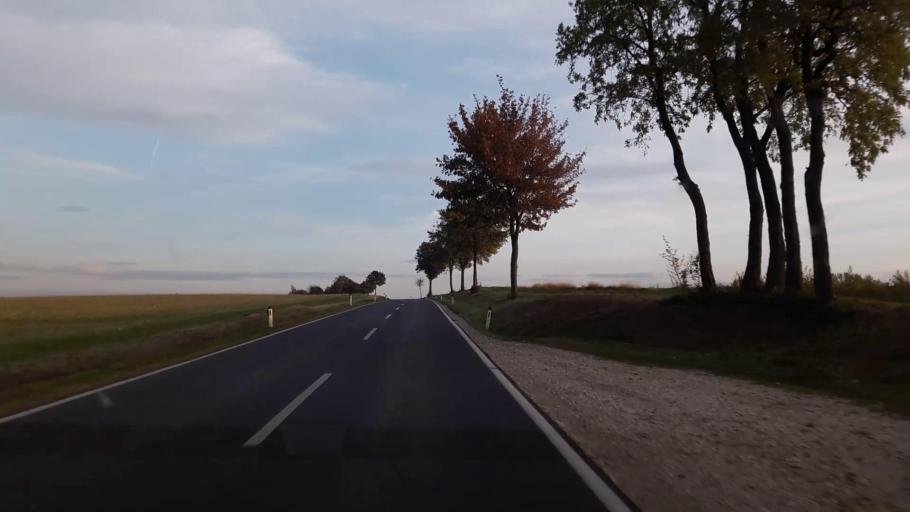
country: AT
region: Lower Austria
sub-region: Politischer Bezirk Korneuburg
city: Grossrussbach
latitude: 48.4416
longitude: 16.3890
